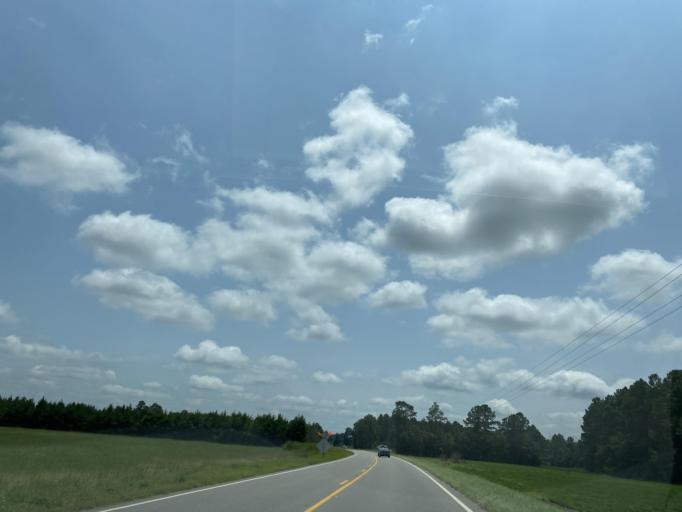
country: US
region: Georgia
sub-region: Jeff Davis County
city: Hazlehurst
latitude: 31.7963
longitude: -82.5657
